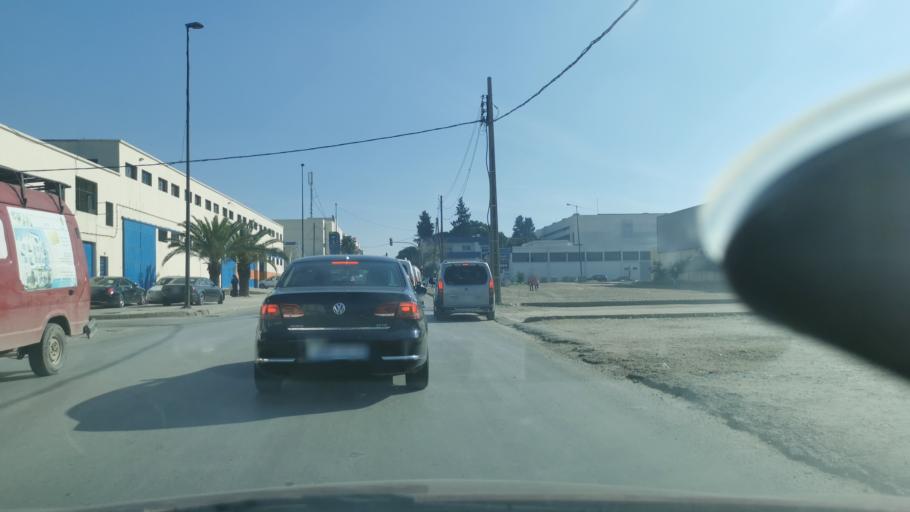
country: MA
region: Fes-Boulemane
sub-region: Fes
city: Fes
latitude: 34.0263
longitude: -4.9774
